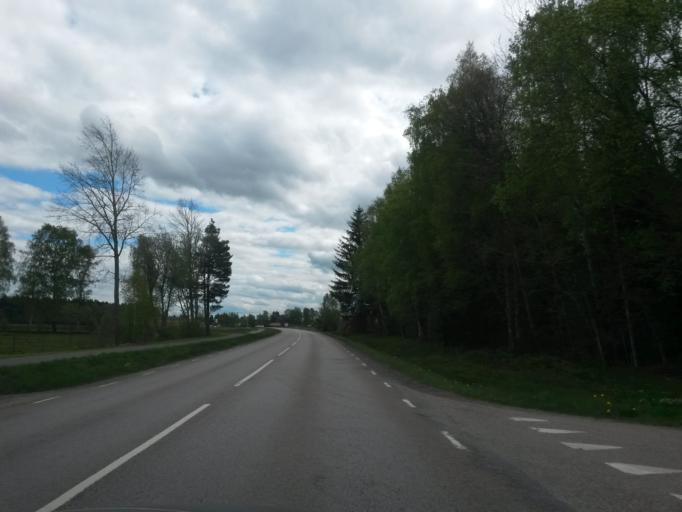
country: SE
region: Vaestra Goetaland
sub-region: Essunga Kommun
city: Nossebro
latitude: 58.2007
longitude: 12.7165
